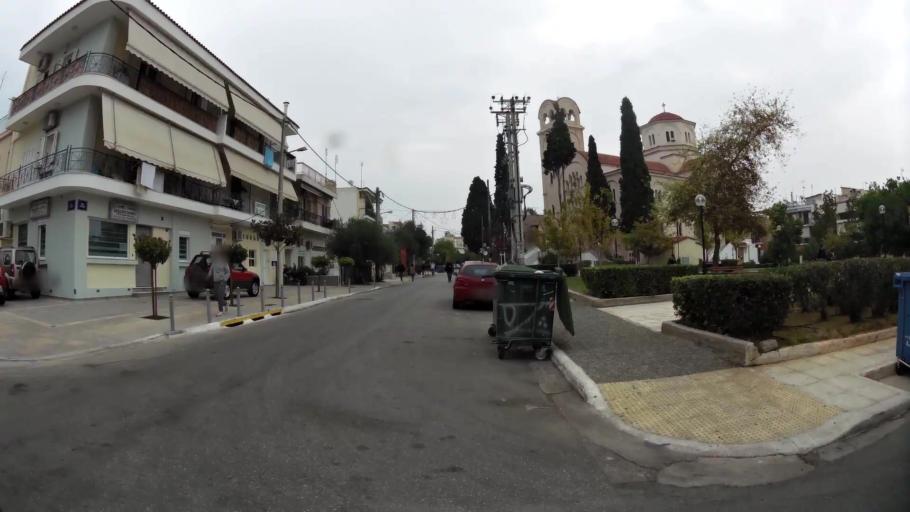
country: GR
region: Attica
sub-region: Nomarchia Athinas
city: Chaidari
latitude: 38.0008
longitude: 23.6723
